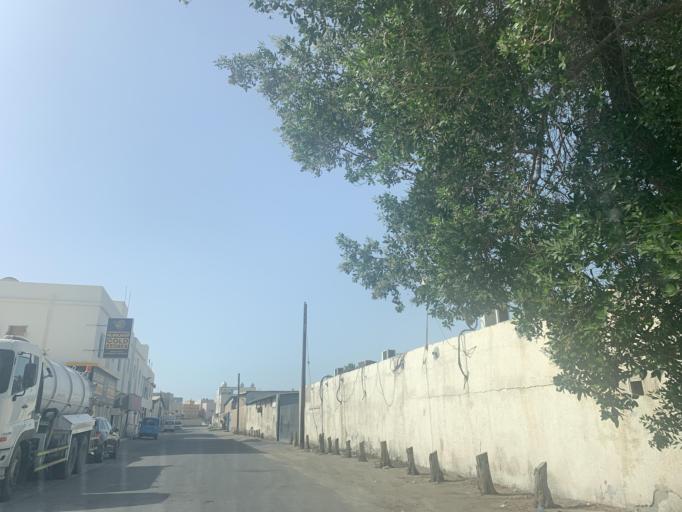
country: BH
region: Northern
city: Sitrah
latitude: 26.1668
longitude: 50.6161
